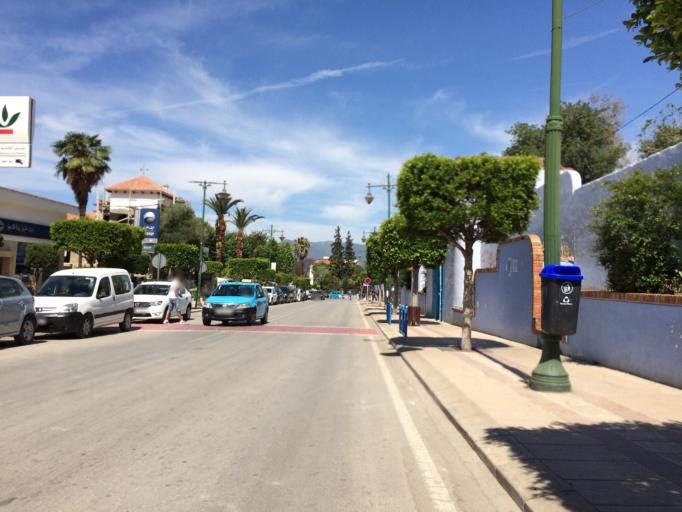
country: MA
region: Tanger-Tetouan
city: Chefchaouene
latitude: 35.1685
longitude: -5.2664
